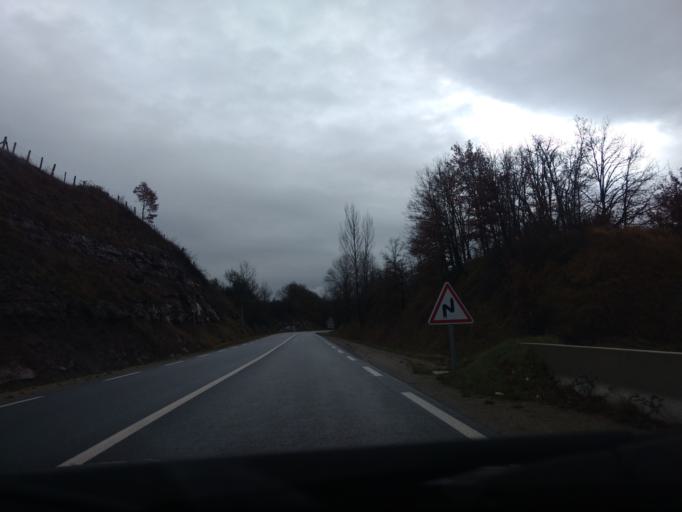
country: FR
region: Midi-Pyrenees
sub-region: Departement de l'Aveyron
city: Firmi
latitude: 44.5113
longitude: 2.3605
